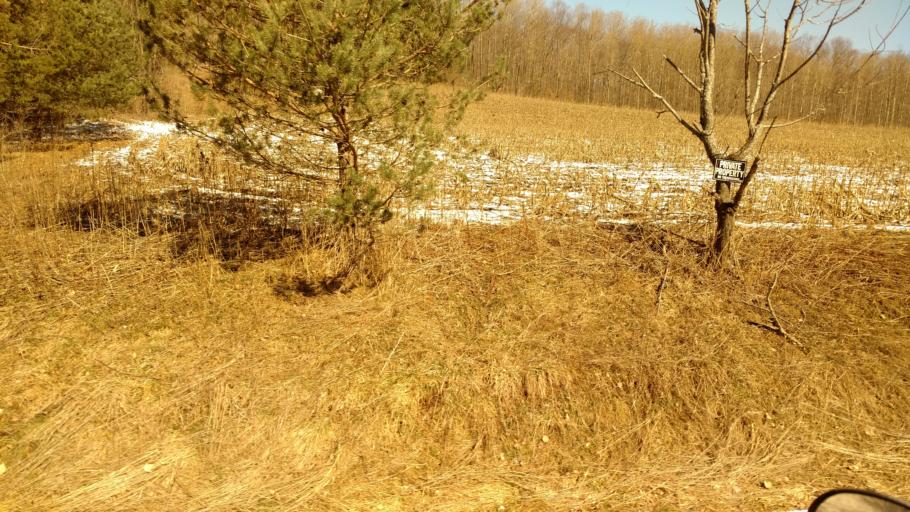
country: US
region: New York
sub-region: Allegany County
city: Wellsville
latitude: 42.0506
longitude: -77.9823
